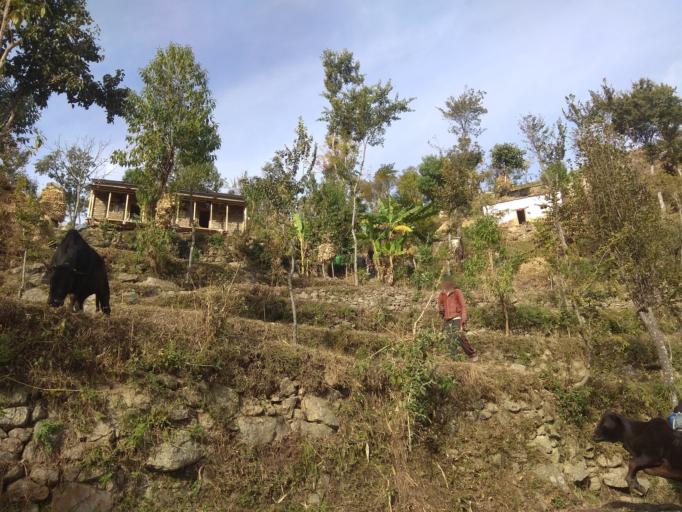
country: NP
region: Mid Western
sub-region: Bheri Zone
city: Dailekh
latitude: 29.2343
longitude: 81.6497
